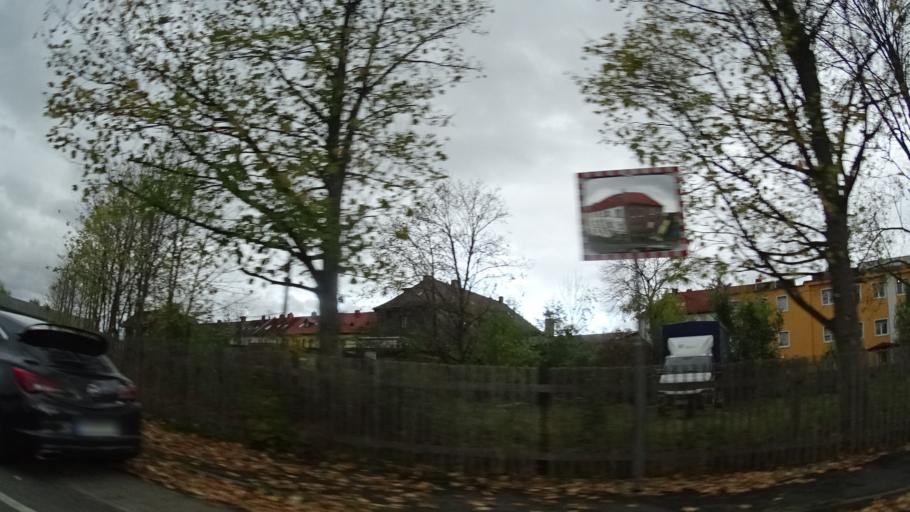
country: DE
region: Thuringia
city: Possneck
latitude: 50.6967
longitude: 11.6038
